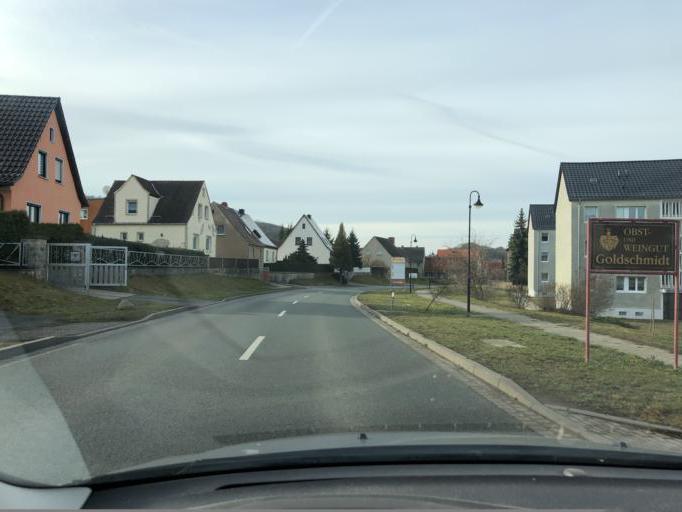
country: DE
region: Saxony-Anhalt
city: Balgstadt
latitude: 51.2063
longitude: 11.7391
